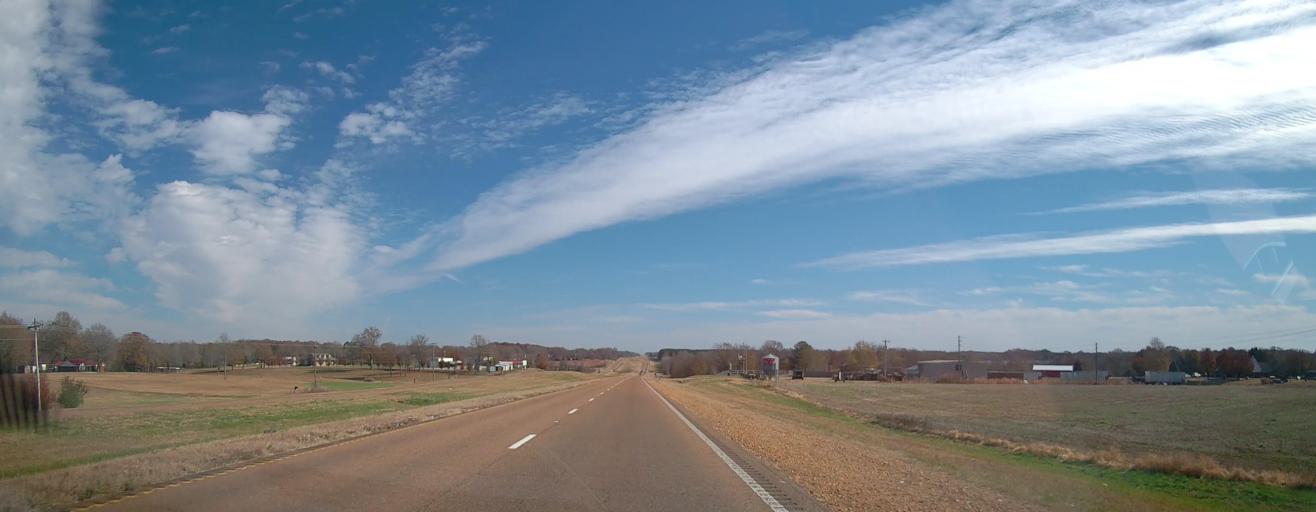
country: US
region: Mississippi
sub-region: Marshall County
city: Holly Springs
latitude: 34.9462
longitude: -89.3860
